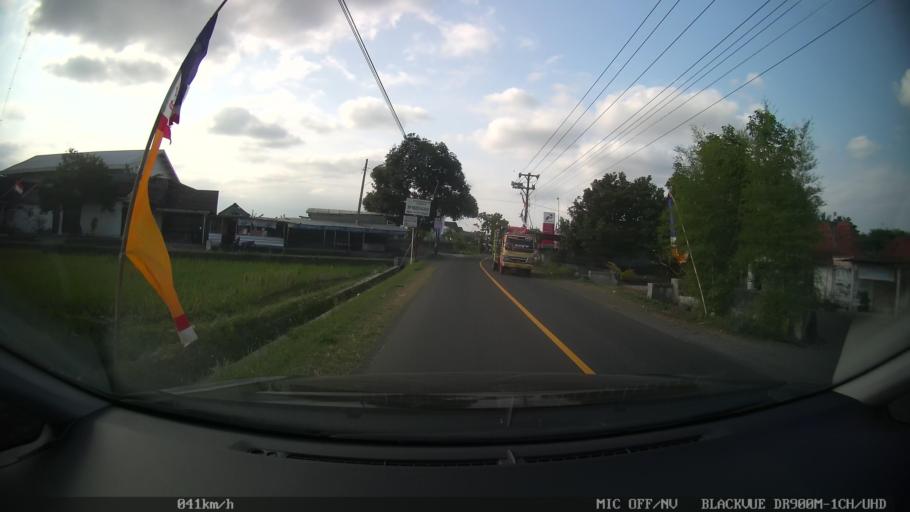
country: ID
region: Central Java
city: Candi Prambanan
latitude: -7.7227
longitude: 110.4724
